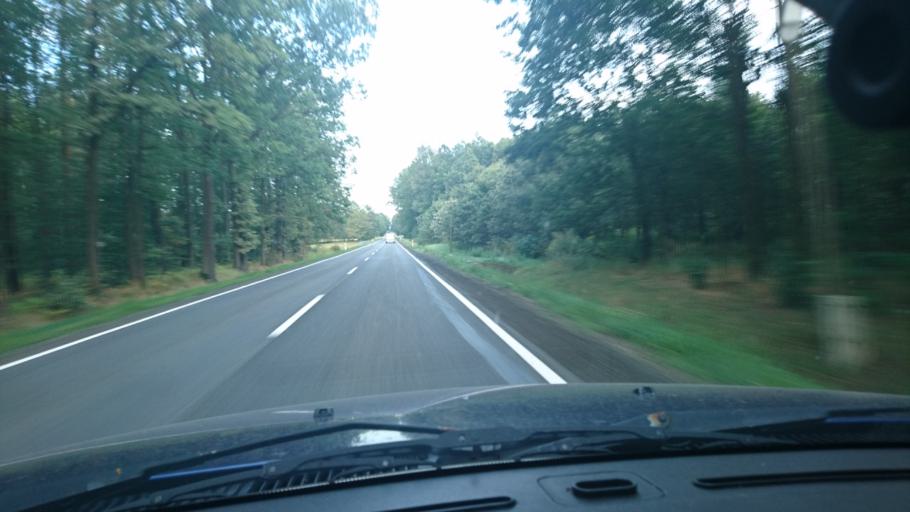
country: PL
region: Opole Voivodeship
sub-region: Powiat oleski
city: Olesno
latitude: 50.8485
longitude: 18.4758
